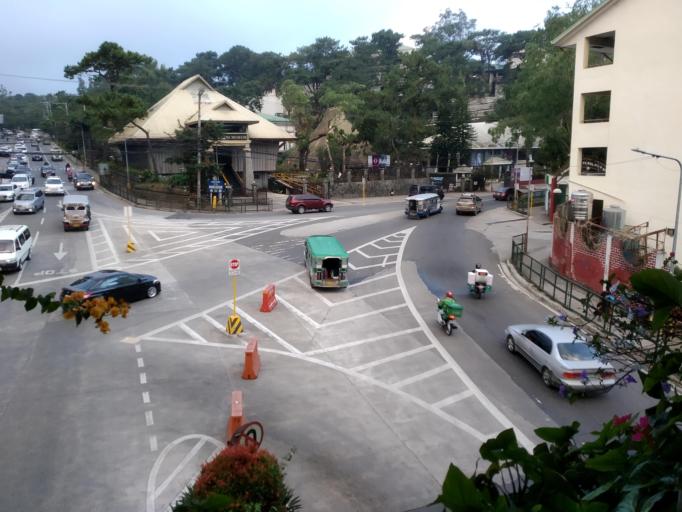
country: PH
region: Cordillera
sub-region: Baguio City
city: Baguio
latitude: 16.4076
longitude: 120.5980
